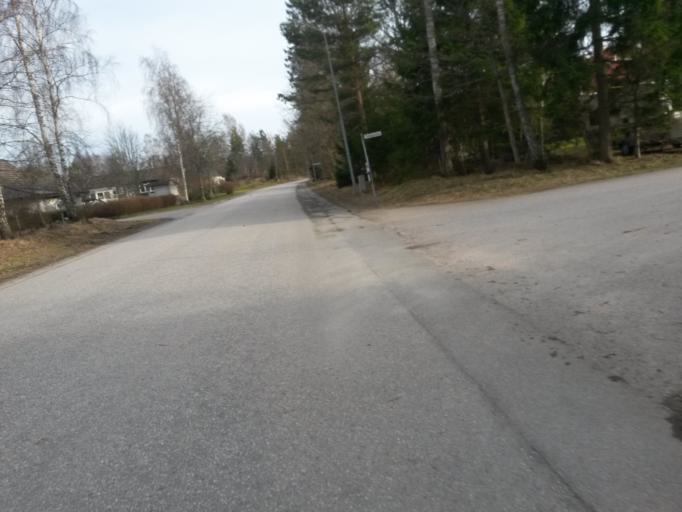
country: SE
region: Vaestra Goetaland
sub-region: Herrljunga Kommun
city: Herrljunga
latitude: 58.0700
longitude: 13.0243
